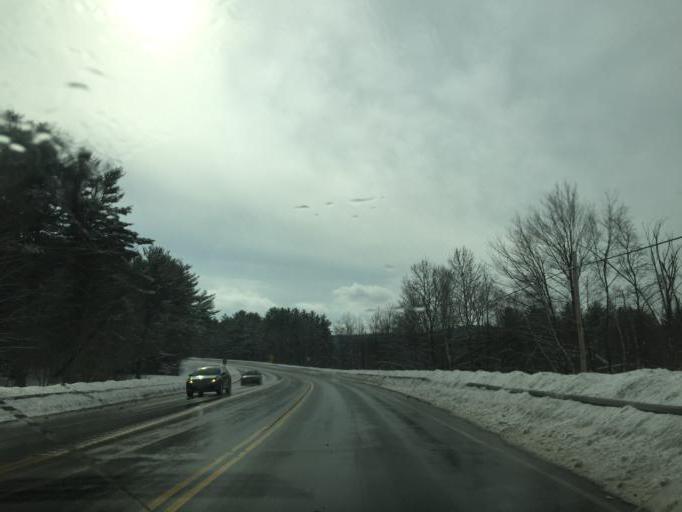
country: US
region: New Hampshire
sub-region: Carroll County
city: Sanbornville
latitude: 43.5494
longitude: -71.0401
